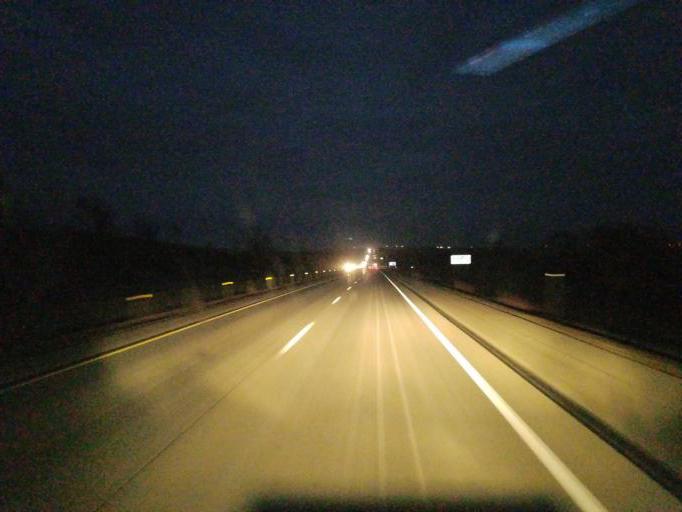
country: US
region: Iowa
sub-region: Guthrie County
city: Stuart
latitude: 41.4960
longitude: -94.4926
